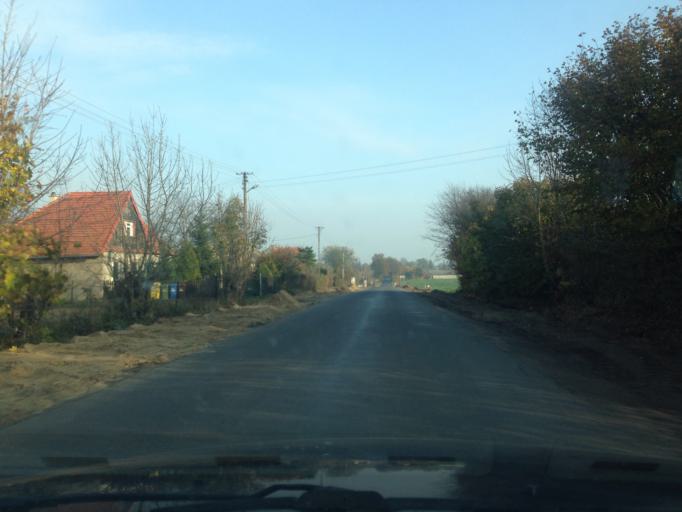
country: PL
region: Kujawsko-Pomorskie
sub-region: Powiat wabrzeski
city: Debowa Laka
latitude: 53.2567
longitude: 19.0984
